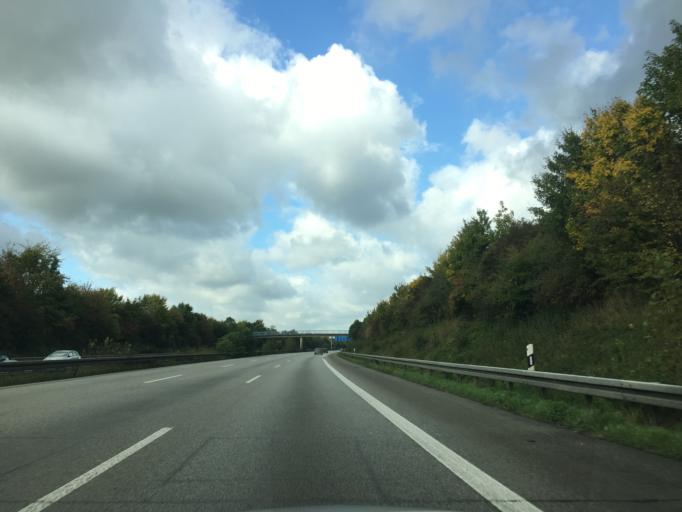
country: DE
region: North Rhine-Westphalia
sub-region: Regierungsbezirk Dusseldorf
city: Meerbusch
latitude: 51.2883
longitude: 6.6723
